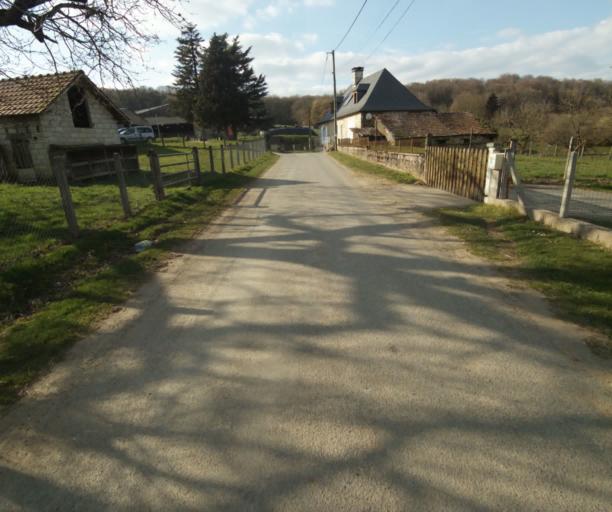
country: FR
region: Limousin
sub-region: Departement de la Correze
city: Saint-Mexant
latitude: 45.3445
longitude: 1.6105
